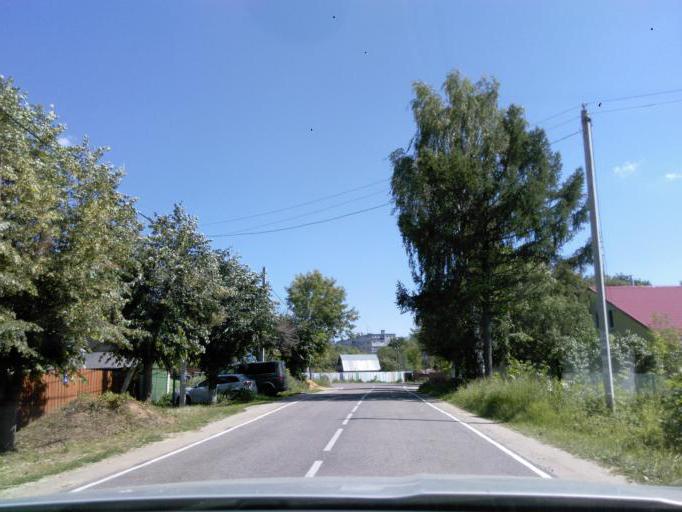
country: RU
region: Moskovskaya
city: Solnechnogorsk
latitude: 56.1817
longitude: 36.9702
